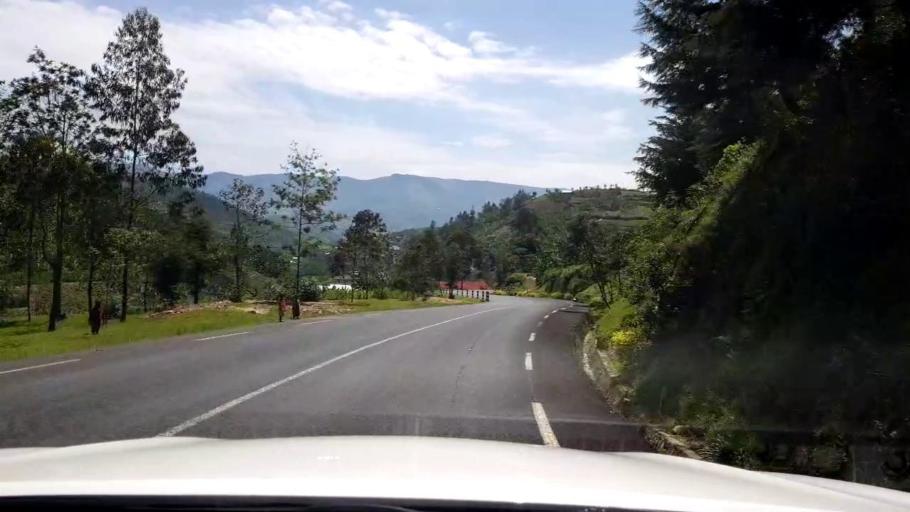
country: RW
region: Southern Province
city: Gitarama
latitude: -1.9184
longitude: 29.6368
